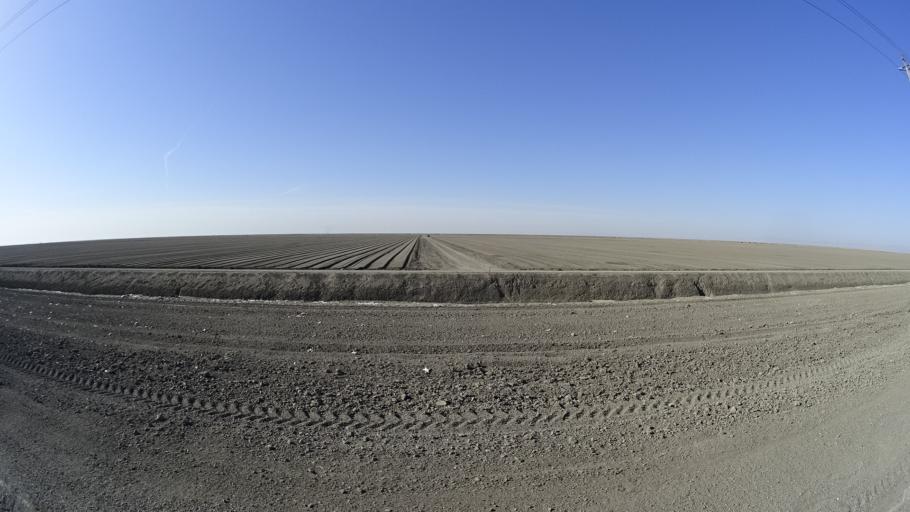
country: US
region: California
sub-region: Kings County
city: Corcoran
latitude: 36.0797
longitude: -119.7068
